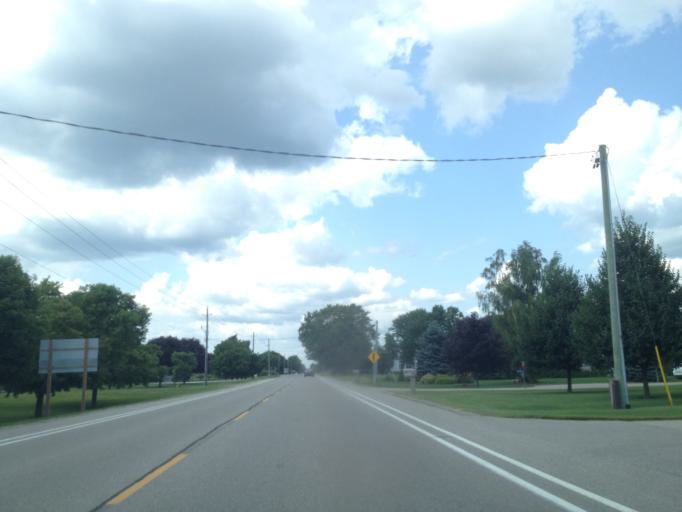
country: CA
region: Ontario
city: Aylmer
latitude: 42.6786
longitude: -80.9854
